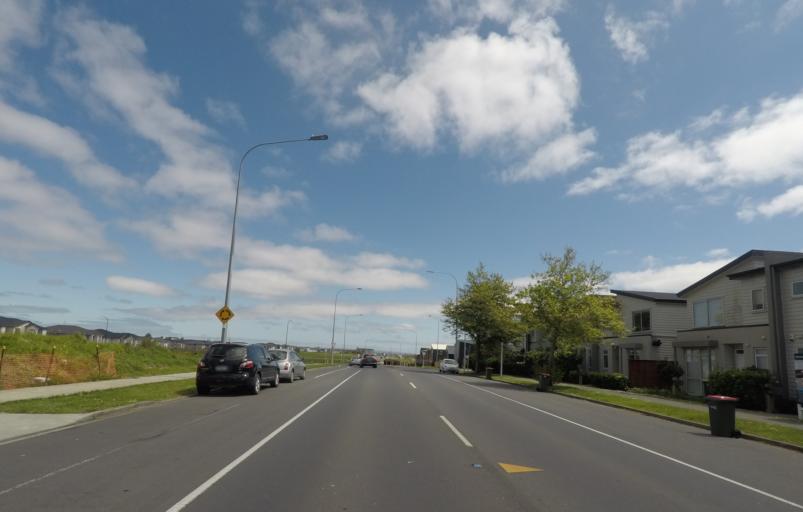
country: NZ
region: Auckland
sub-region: Auckland
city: Manukau City
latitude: -36.9735
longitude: 174.9139
